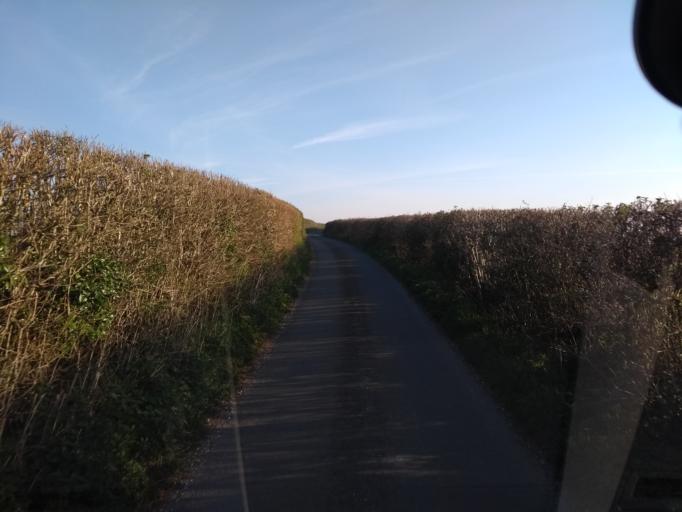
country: GB
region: England
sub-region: Somerset
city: Crewkerne
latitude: 50.8558
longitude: -2.8139
